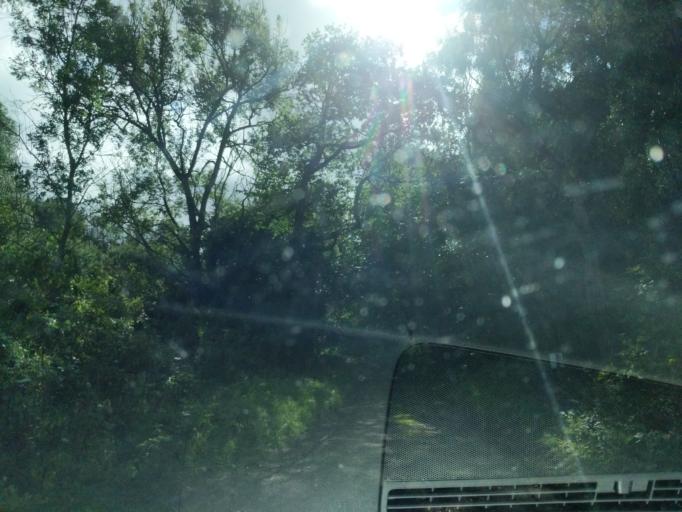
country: GB
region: Scotland
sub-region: The Scottish Borders
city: Kelso
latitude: 55.5677
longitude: -2.4729
